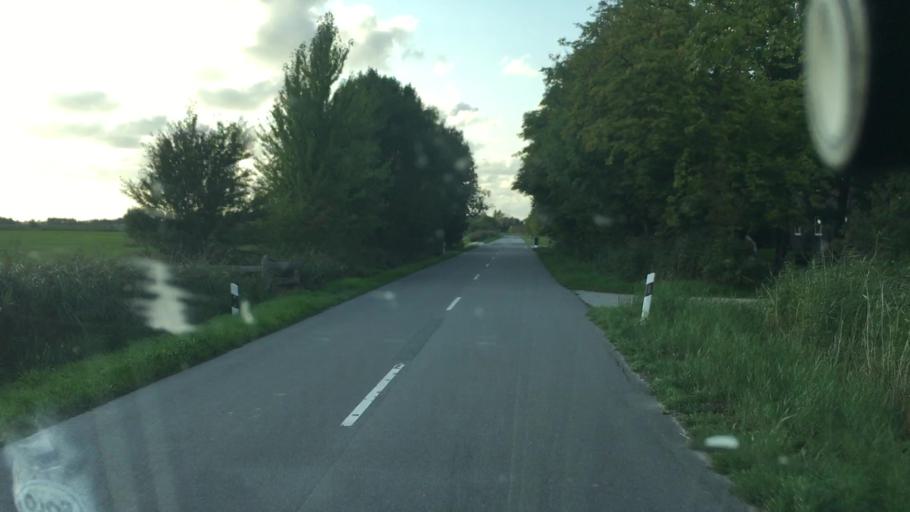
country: DE
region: Lower Saxony
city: Werdum
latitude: 53.6779
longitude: 7.7154
